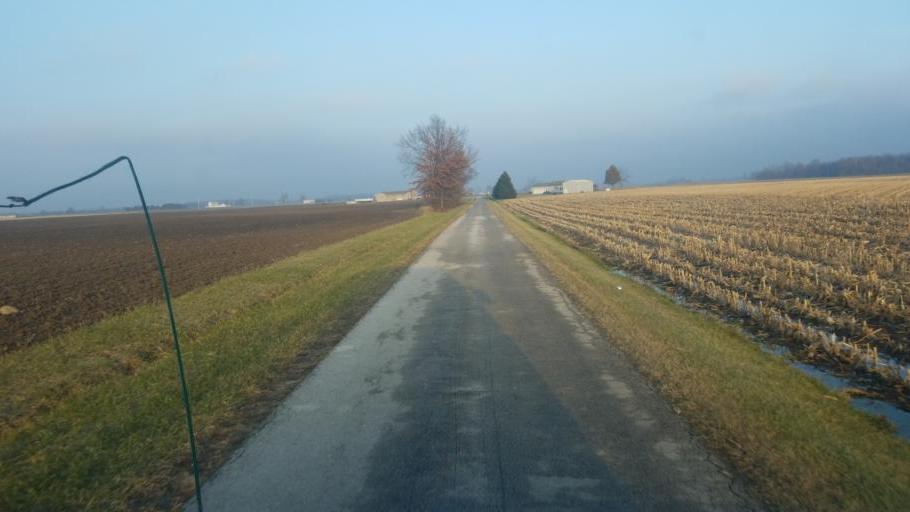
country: US
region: Ohio
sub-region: Wyandot County
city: Carey
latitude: 40.9248
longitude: -83.4330
